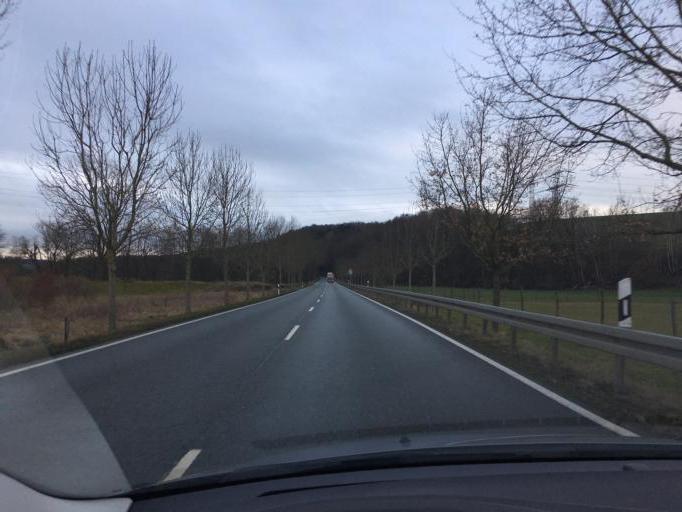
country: DE
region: Thuringia
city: Juckelberg
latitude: 50.8941
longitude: 12.6292
